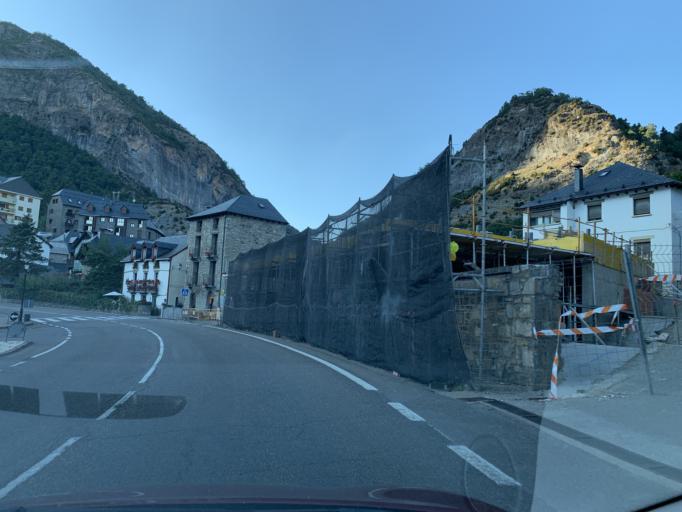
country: ES
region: Aragon
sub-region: Provincia de Huesca
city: Sallent de Gallego
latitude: 42.7352
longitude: -0.3121
